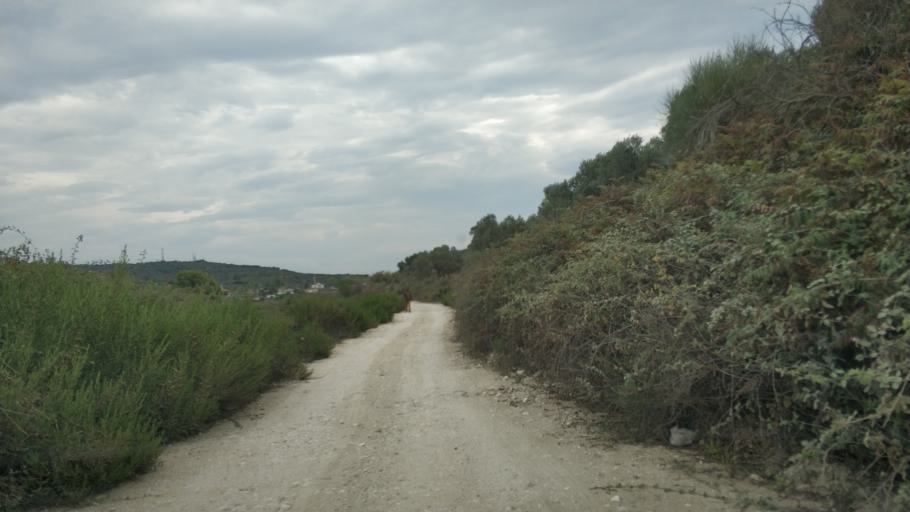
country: AL
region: Vlore
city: Vlore
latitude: 40.5114
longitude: 19.4025
